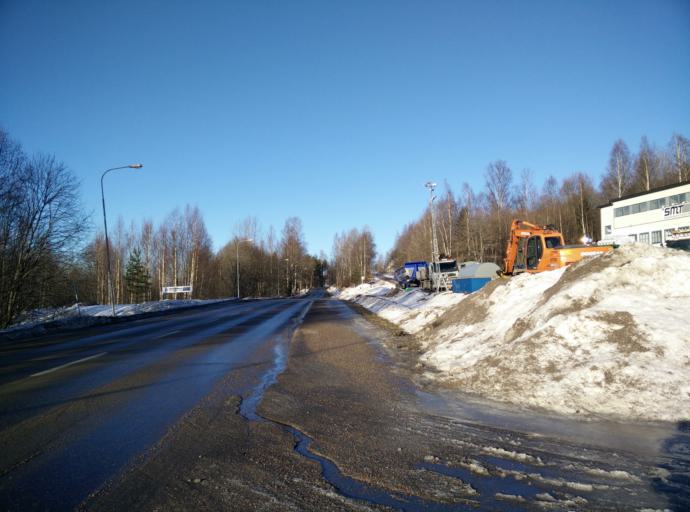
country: SE
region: Vaesternorrland
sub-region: Sundsvalls Kommun
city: Skottsund
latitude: 62.3146
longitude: 17.3930
